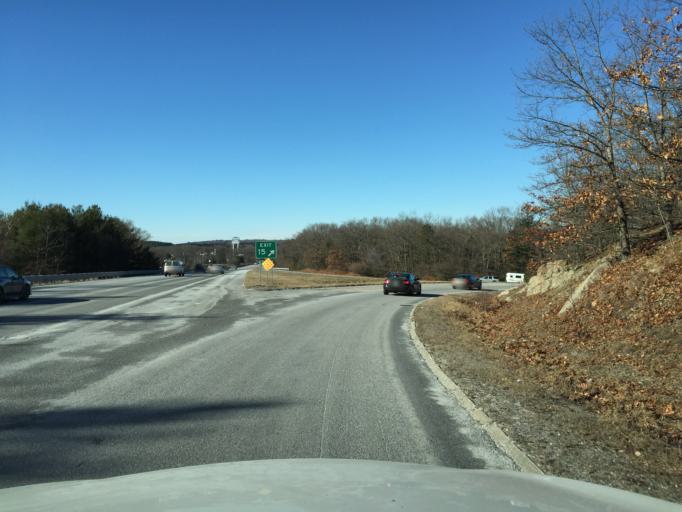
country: US
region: Massachusetts
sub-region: Norfolk County
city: Wrentham
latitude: 42.0401
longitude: -71.3410
